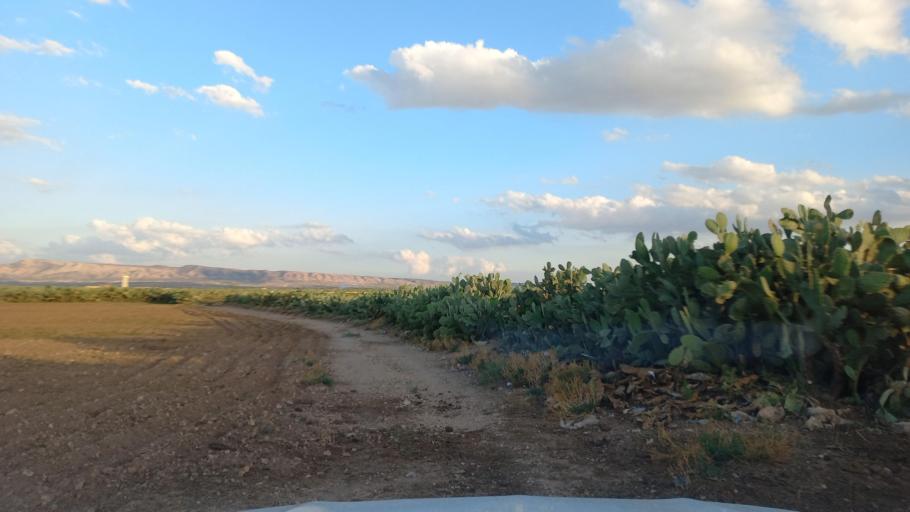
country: TN
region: Al Qasrayn
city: Sbiba
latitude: 35.3756
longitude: 9.0499
